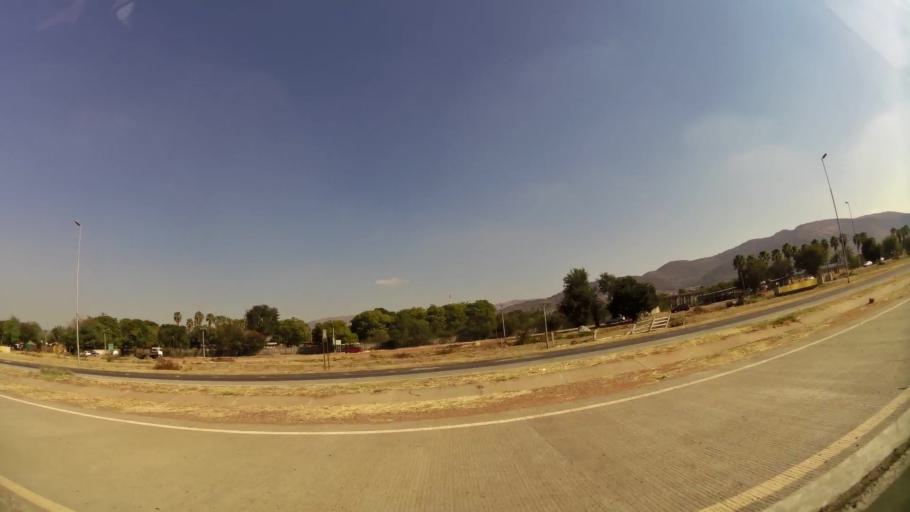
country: ZA
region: North-West
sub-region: Bojanala Platinum District Municipality
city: Rustenburg
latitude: -25.6511
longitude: 27.2164
